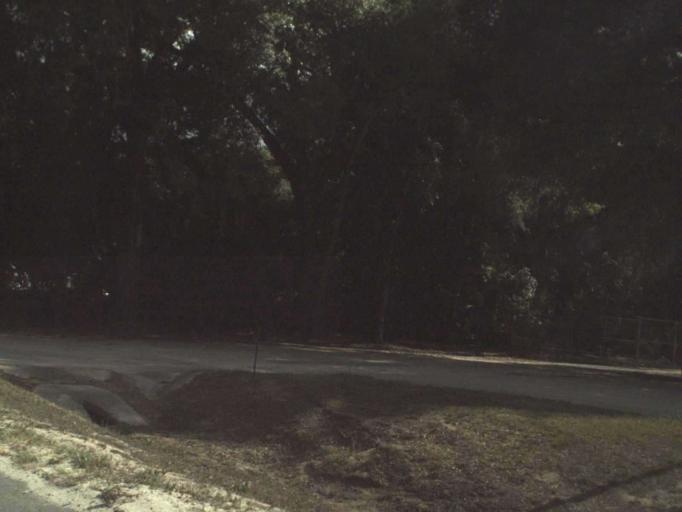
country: US
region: Florida
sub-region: Marion County
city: Belleview
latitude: 29.0689
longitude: -82.0536
